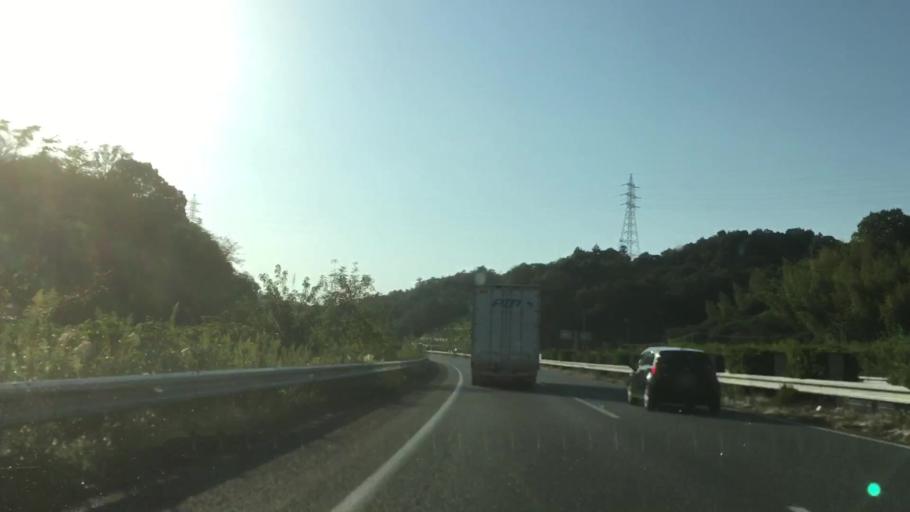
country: JP
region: Yamaguchi
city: Ogori-shimogo
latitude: 34.1264
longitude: 131.4031
